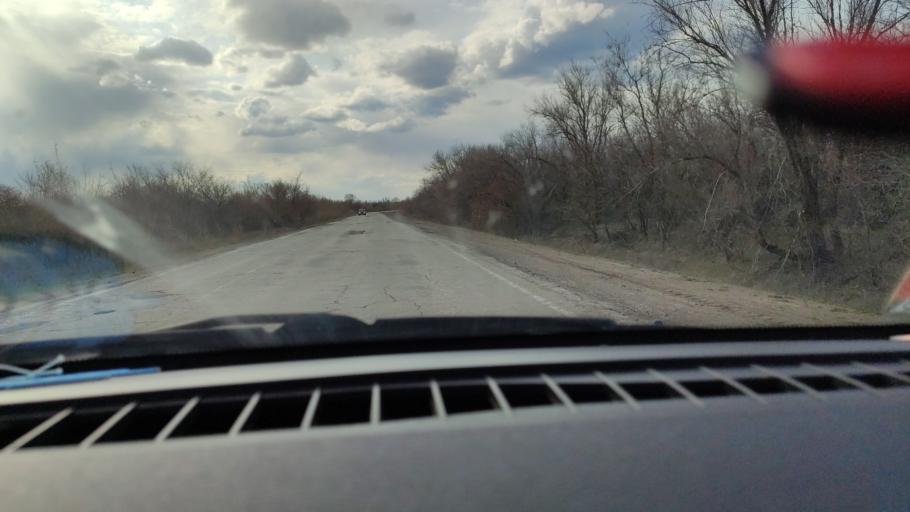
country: RU
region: Saratov
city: Krasnoarmeysk
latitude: 51.0721
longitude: 45.9850
